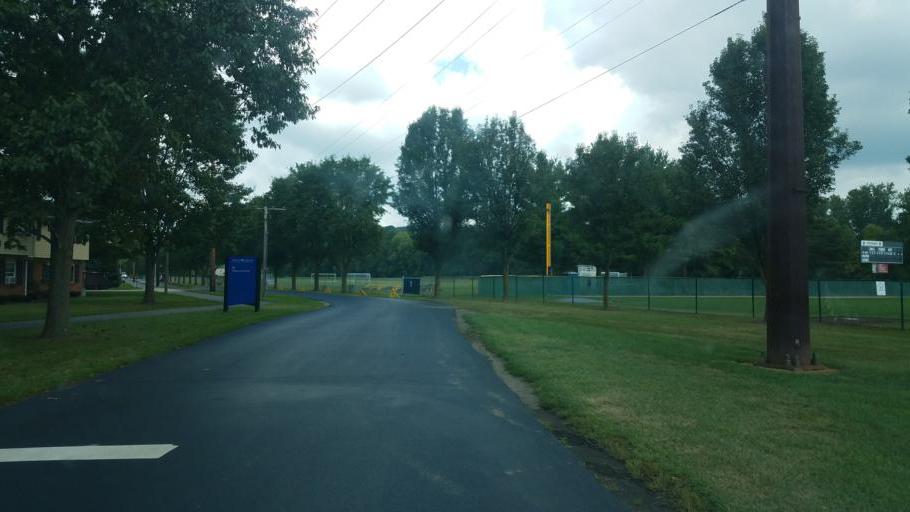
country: US
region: Ohio
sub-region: Knox County
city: Mount Vernon
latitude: 40.3741
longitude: -82.4688
